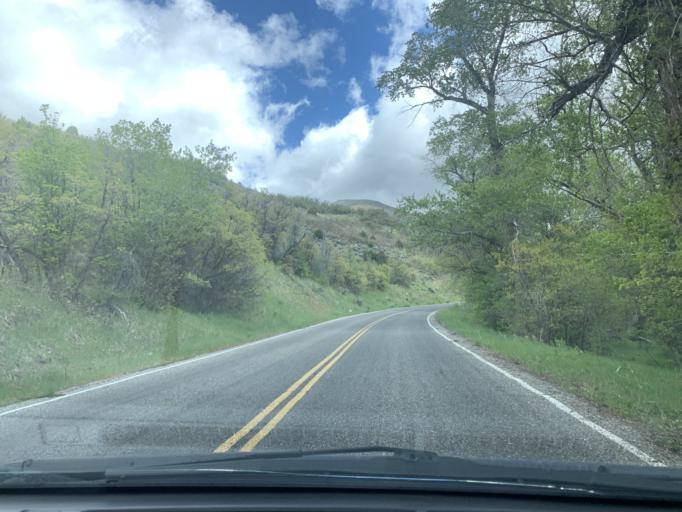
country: US
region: Utah
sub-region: Juab County
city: Nephi
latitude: 39.7724
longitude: -111.7043
